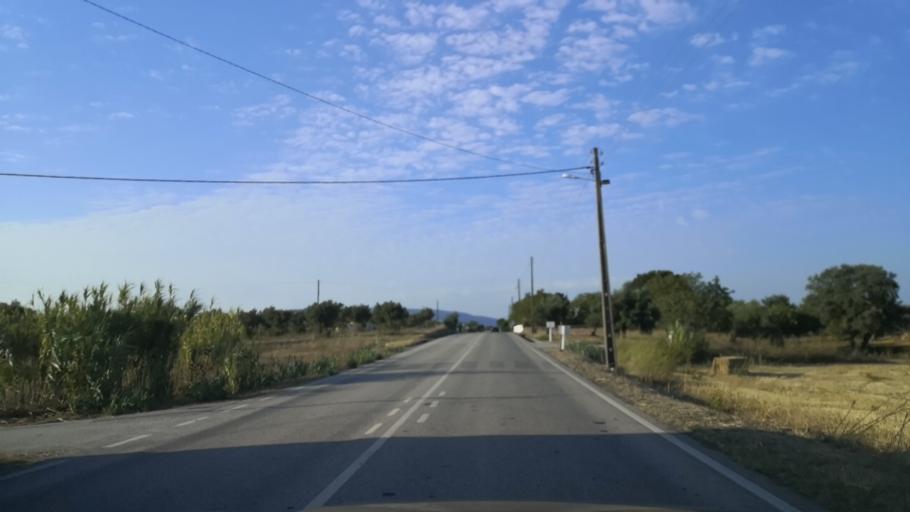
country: PT
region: Santarem
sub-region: Alcanena
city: Alcanena
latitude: 39.4136
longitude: -8.6375
